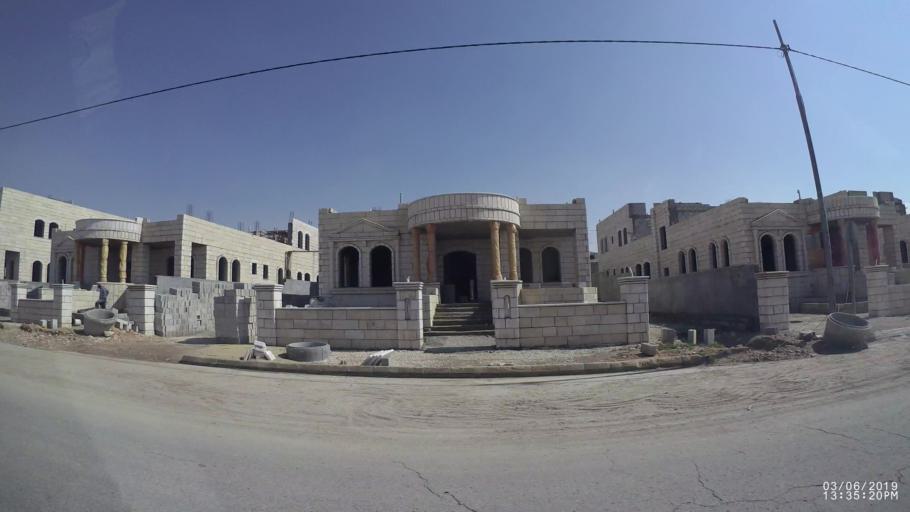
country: JO
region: Zarqa
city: Zarqa
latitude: 32.0760
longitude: 36.1082
